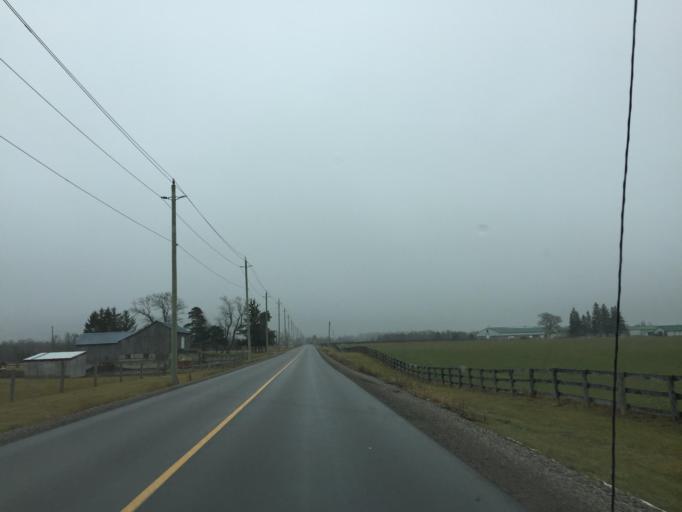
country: CA
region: Ontario
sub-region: Wellington County
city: Guelph
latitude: 43.4734
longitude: -80.3320
